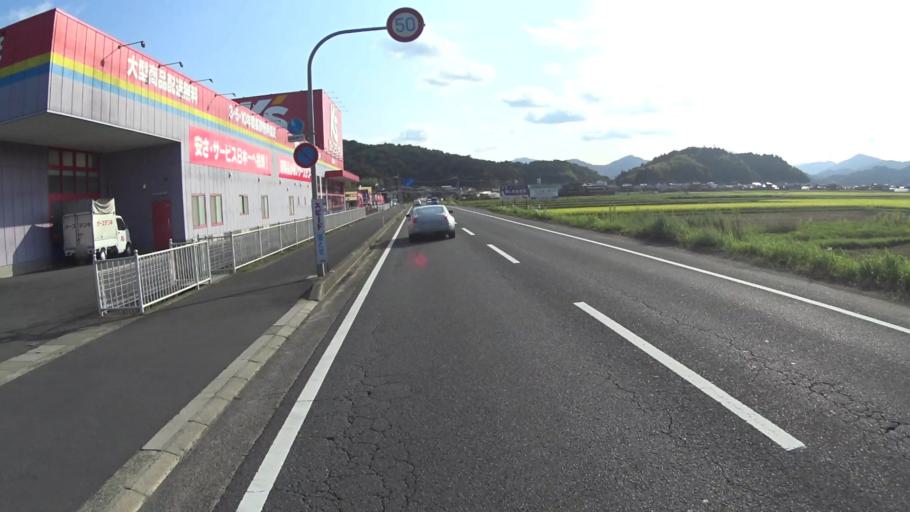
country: JP
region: Kyoto
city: Miyazu
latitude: 35.5300
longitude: 135.1209
